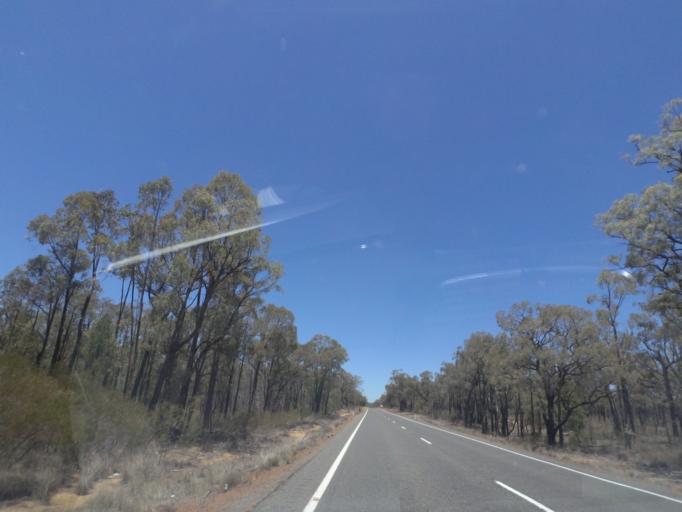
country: AU
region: New South Wales
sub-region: Narrabri
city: Narrabri
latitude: -30.7097
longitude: 149.5306
